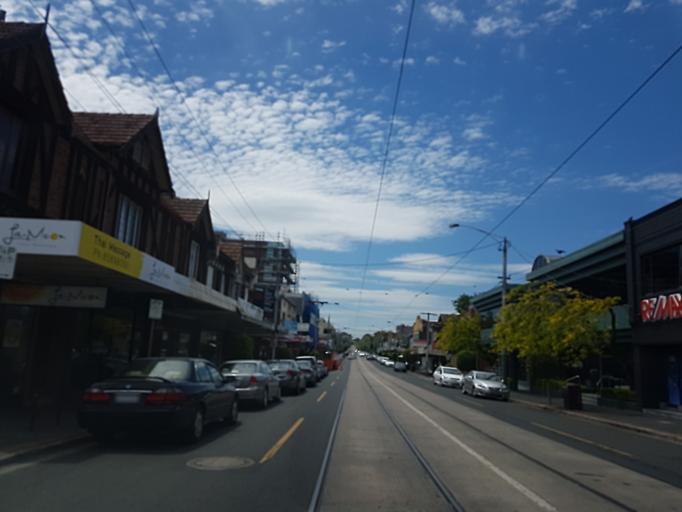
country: AU
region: Victoria
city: Caulfield North
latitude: -37.8746
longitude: 145.0243
